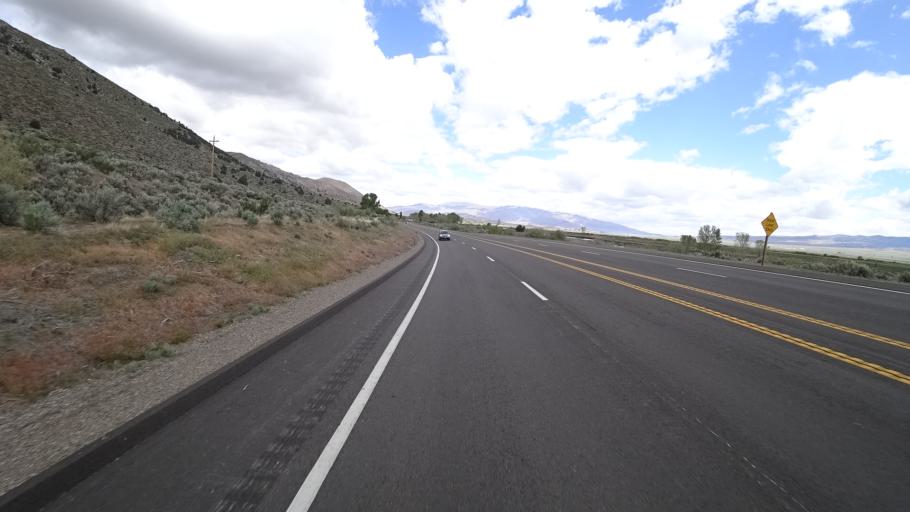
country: US
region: Nevada
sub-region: Lyon County
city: Smith Valley
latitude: 38.6018
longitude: -119.5188
